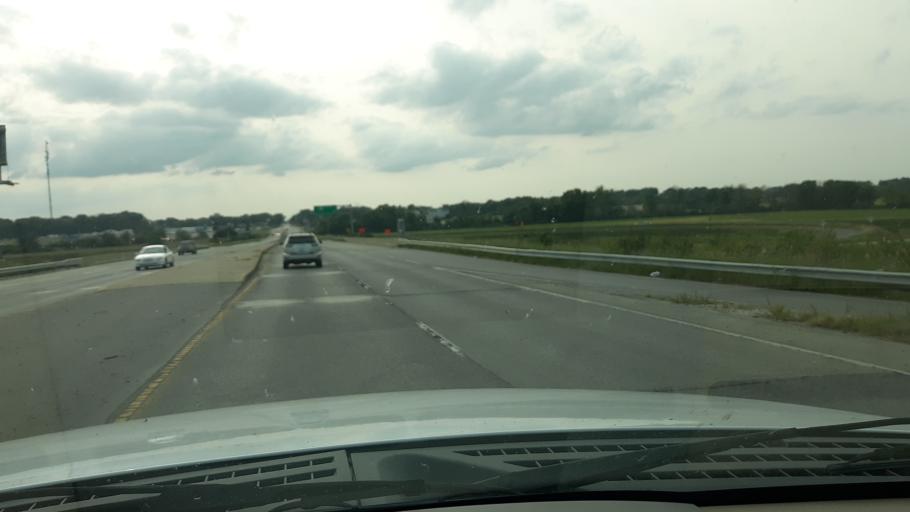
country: US
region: Indiana
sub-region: Gibson County
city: Princeton
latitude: 38.3555
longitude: -87.5970
